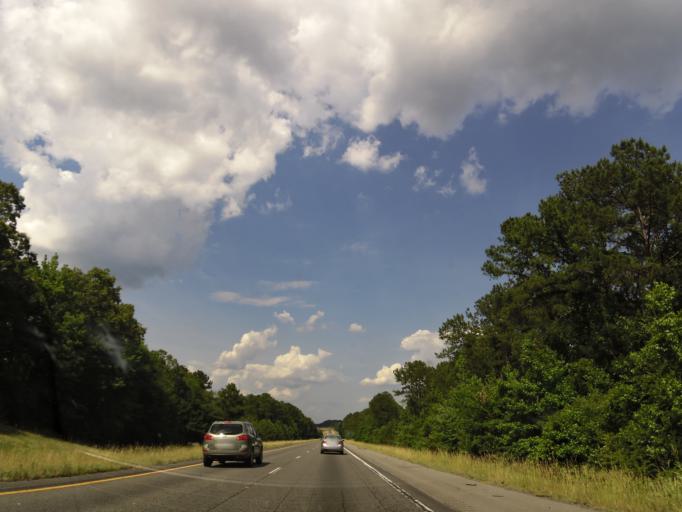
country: US
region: Alabama
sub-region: Hale County
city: Moundville
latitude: 33.0499
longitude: -87.7200
